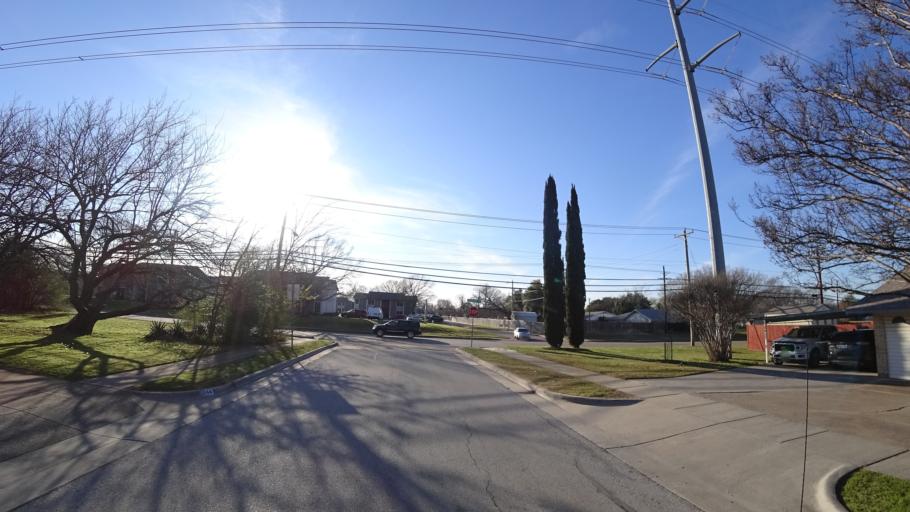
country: US
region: Texas
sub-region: Denton County
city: Lewisville
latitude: 33.0372
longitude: -97.0098
